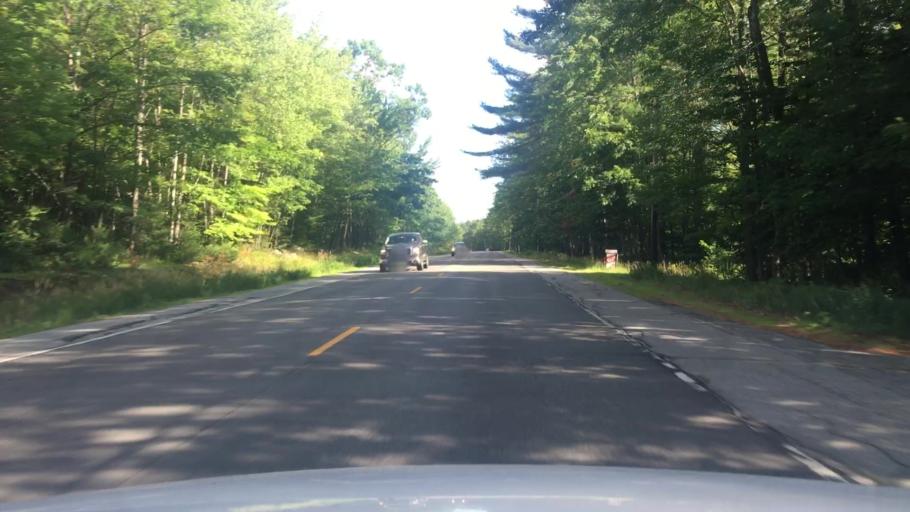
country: US
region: Maine
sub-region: Franklin County
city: Jay
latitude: 44.5362
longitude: -70.2338
